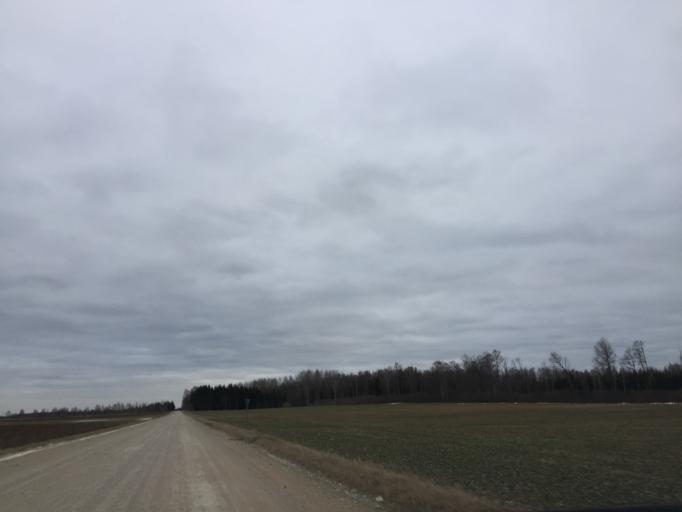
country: LT
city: Zagare
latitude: 56.3091
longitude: 23.2544
